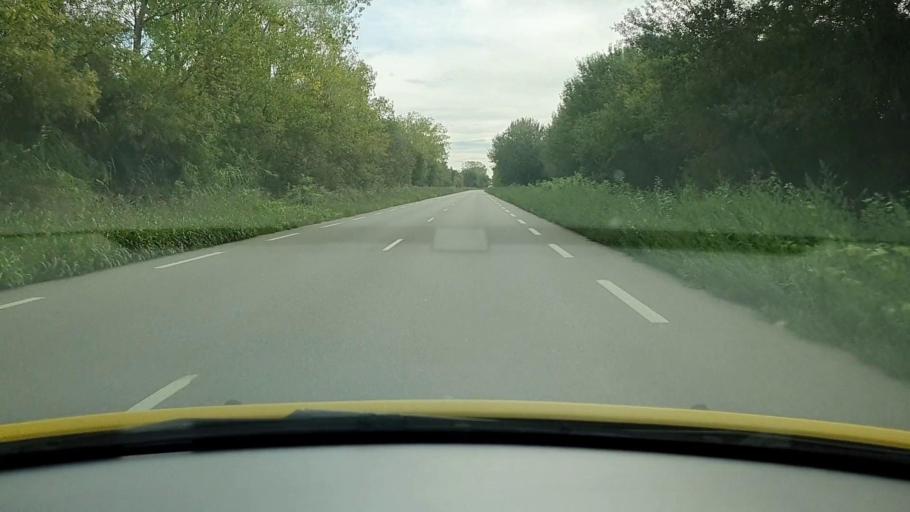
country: FR
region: Languedoc-Roussillon
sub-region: Departement du Gard
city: Bellegarde
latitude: 43.7417
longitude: 4.5060
